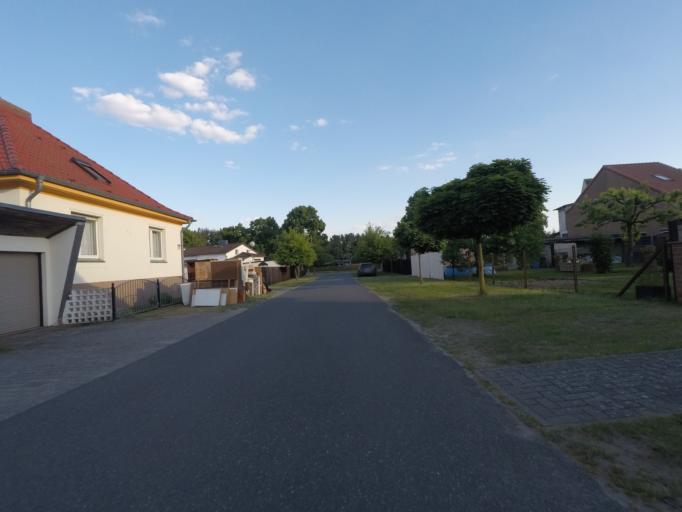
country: DE
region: Brandenburg
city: Marienwerder
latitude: 52.8544
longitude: 13.6725
